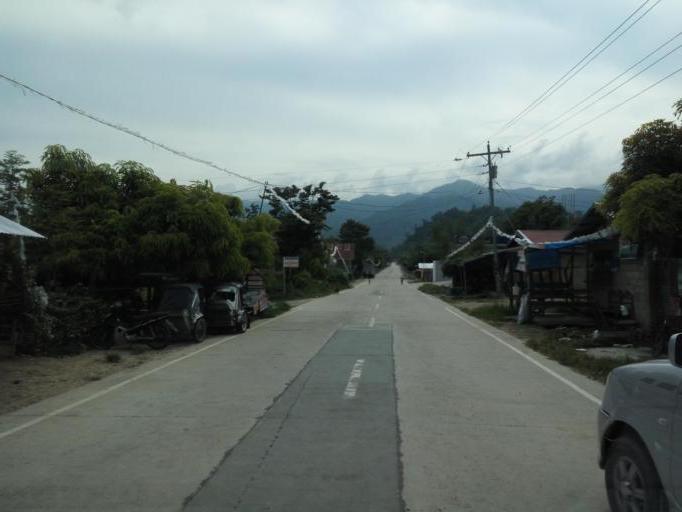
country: PH
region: Central Luzon
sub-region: Province of Aurora
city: Dinalongan
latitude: 16.0773
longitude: 121.7673
